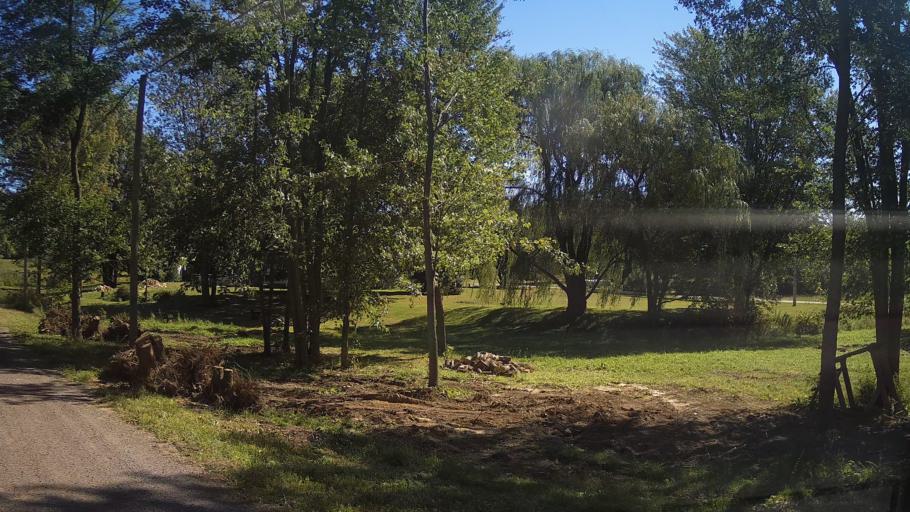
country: CA
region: Ontario
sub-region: Lanark County
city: Smiths Falls
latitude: 44.8389
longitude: -75.8850
